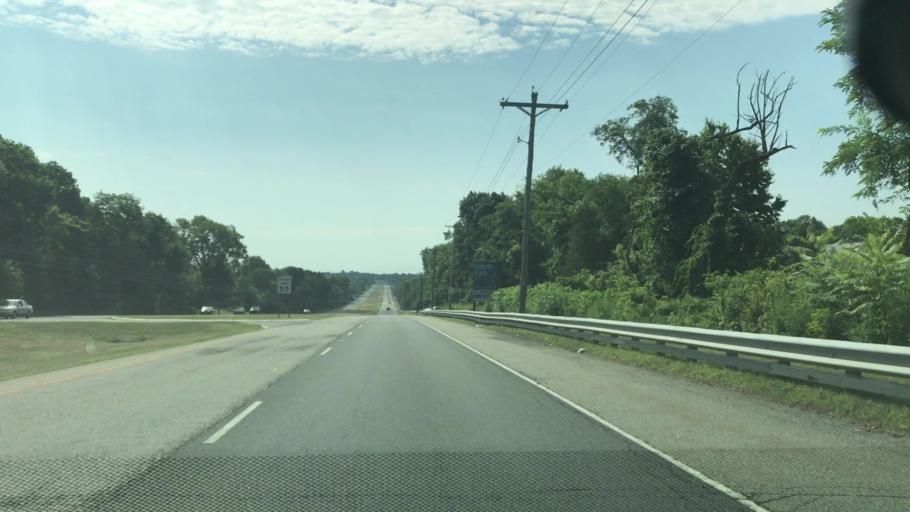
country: US
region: New Jersey
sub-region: Hunterdon County
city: Whitehouse Station
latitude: 40.6393
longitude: -74.7941
